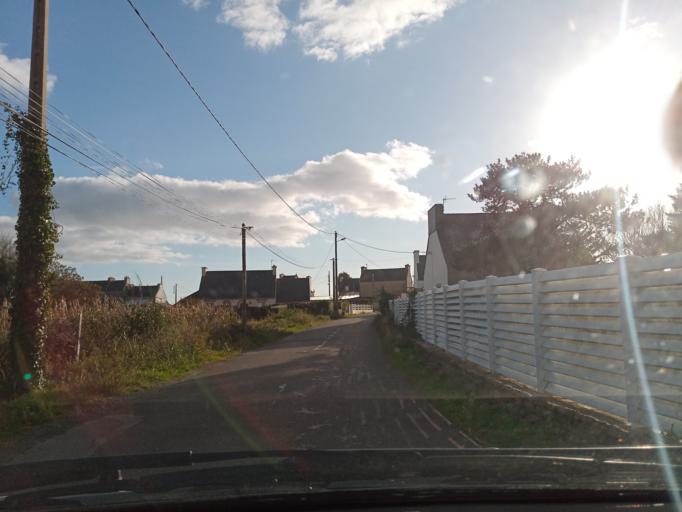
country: FR
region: Brittany
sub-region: Departement du Finistere
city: Audierne
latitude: 48.0181
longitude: -4.5168
